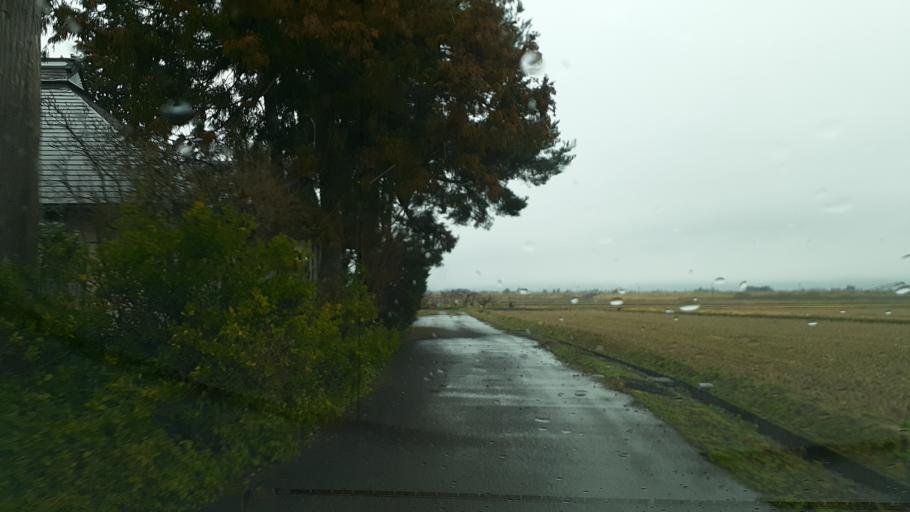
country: JP
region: Fukushima
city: Kitakata
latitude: 37.5845
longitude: 139.8568
